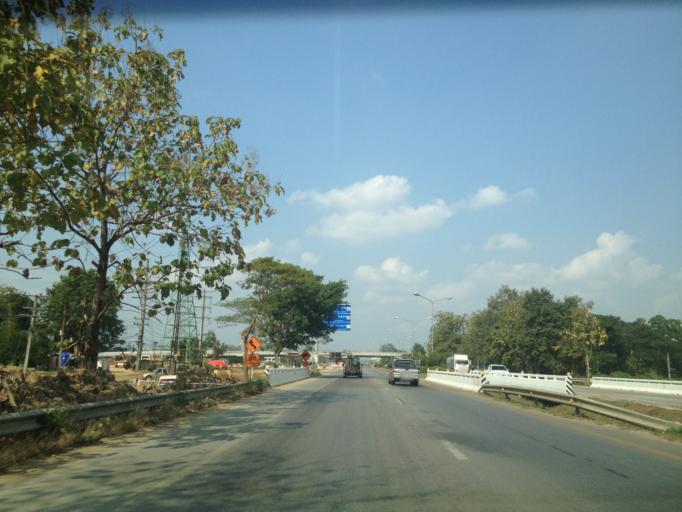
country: TH
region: Chiang Mai
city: Saraphi
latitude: 18.7325
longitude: 99.0382
